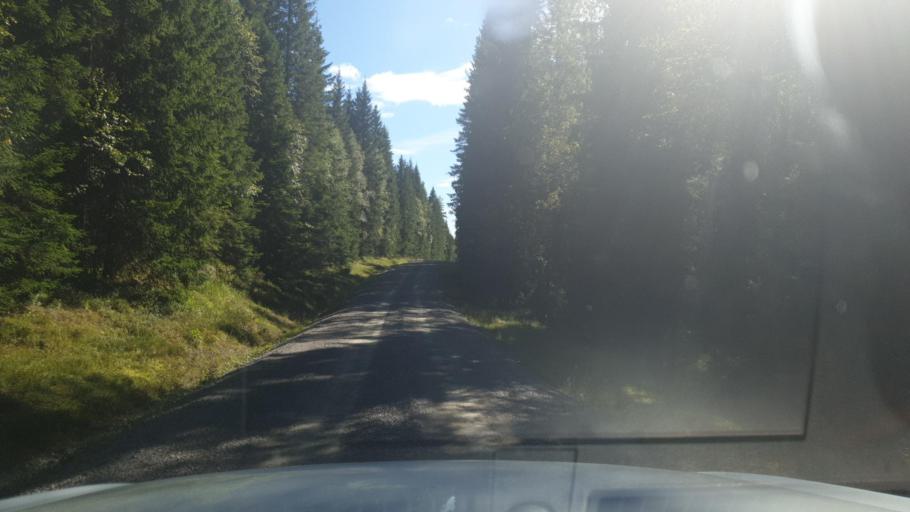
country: SE
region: Vaermland
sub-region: Eda Kommun
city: Charlottenberg
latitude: 60.0684
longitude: 12.6232
